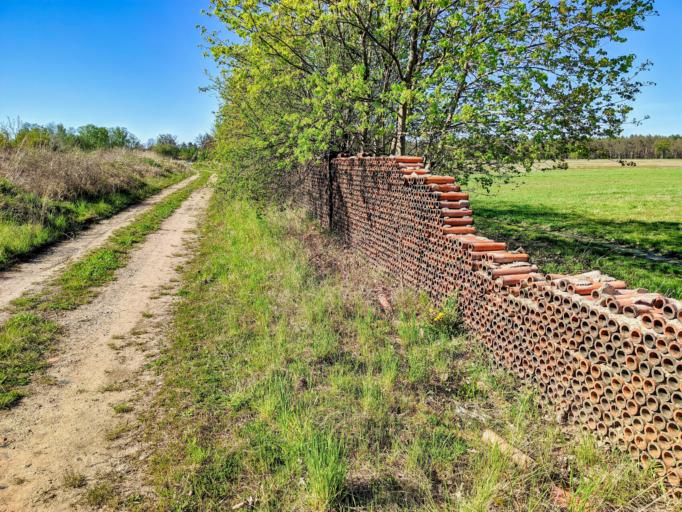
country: PL
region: Lubusz
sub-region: Powiat zarski
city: Kunice Zarskie
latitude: 51.5678
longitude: 15.1846
